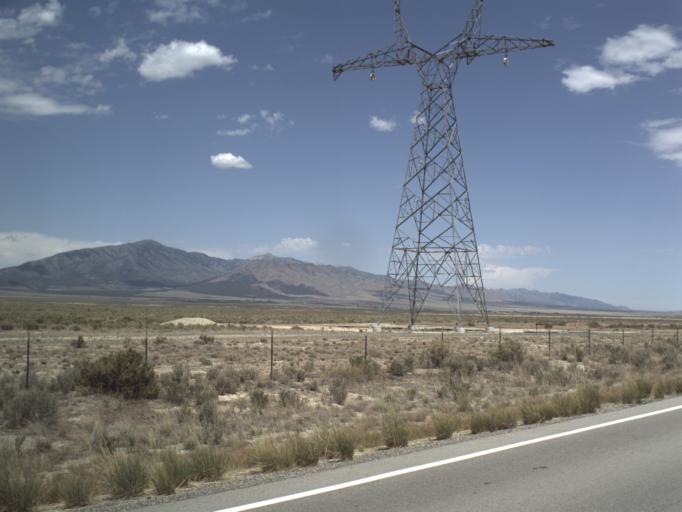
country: US
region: Utah
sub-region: Tooele County
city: Tooele
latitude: 40.2643
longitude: -112.3976
